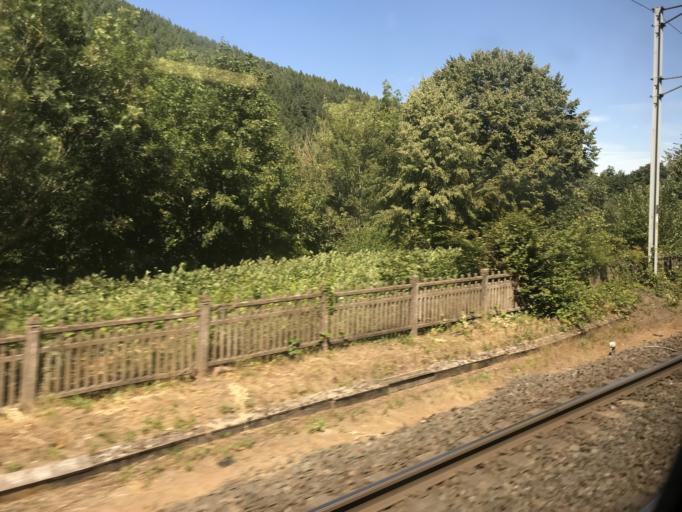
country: FR
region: Alsace
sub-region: Departement du Bas-Rhin
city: Saverne
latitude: 48.7202
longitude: 7.3146
